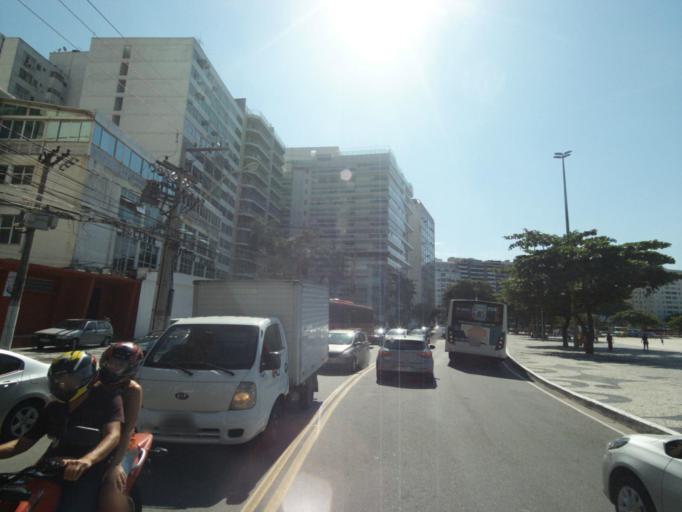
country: BR
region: Rio de Janeiro
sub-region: Niteroi
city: Niteroi
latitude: -22.9041
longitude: -43.1179
